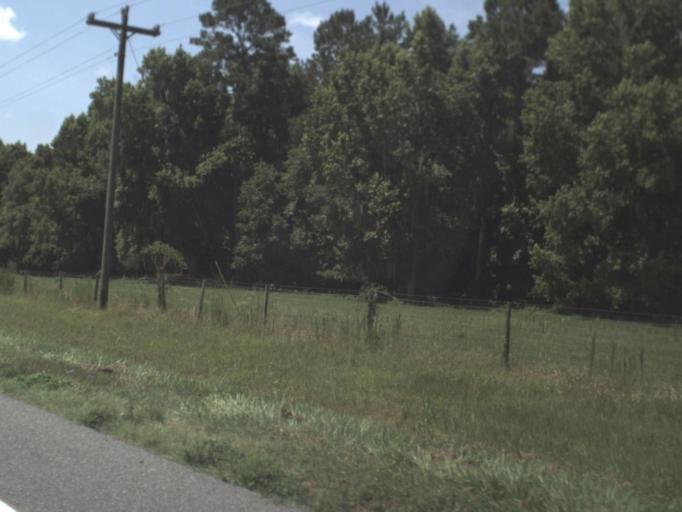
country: US
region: Florida
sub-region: Levy County
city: Williston
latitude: 29.4624
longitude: -82.4142
